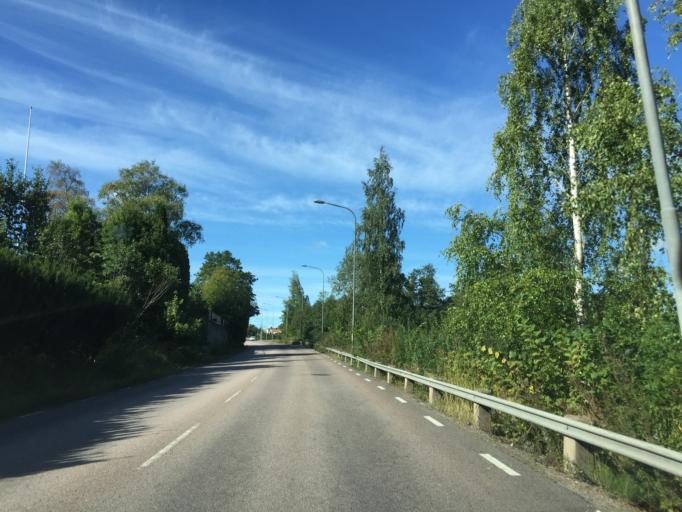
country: SE
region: Vaestmanland
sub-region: Vasteras
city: Vasteras
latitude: 59.6146
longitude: 16.5318
